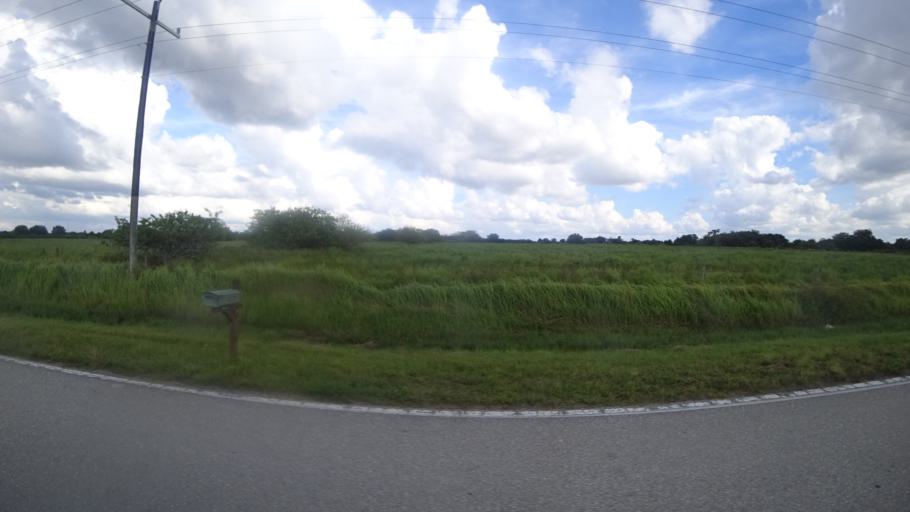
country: US
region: Florida
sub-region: Manatee County
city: Memphis
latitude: 27.6130
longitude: -82.5274
